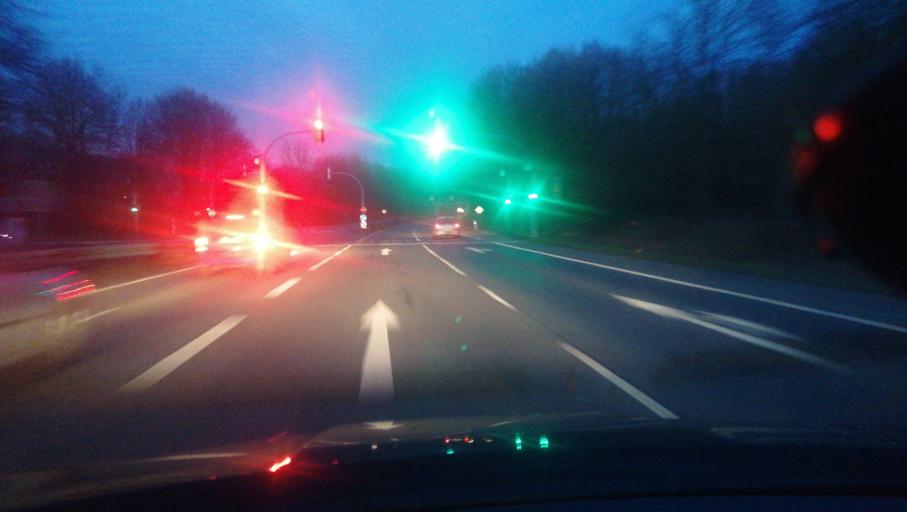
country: DE
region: North Rhine-Westphalia
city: Waltrop
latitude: 51.5565
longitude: 7.3992
